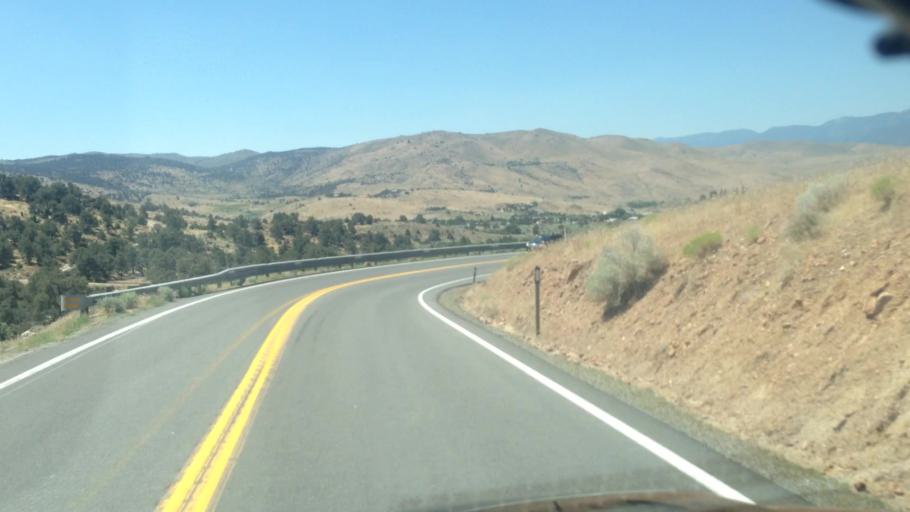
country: US
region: Nevada
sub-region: Storey County
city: Virginia City
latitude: 39.3843
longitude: -119.7123
